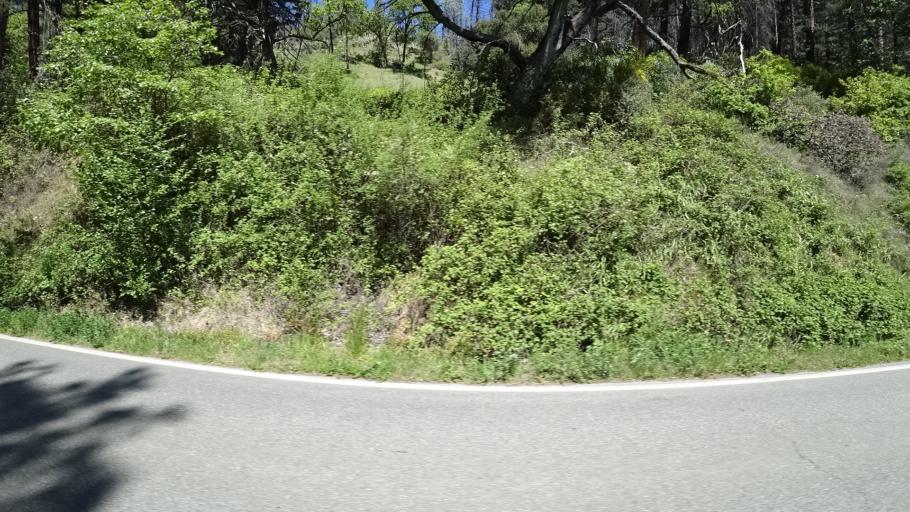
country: US
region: California
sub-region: Trinity County
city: Hayfork
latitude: 40.7485
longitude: -123.2732
